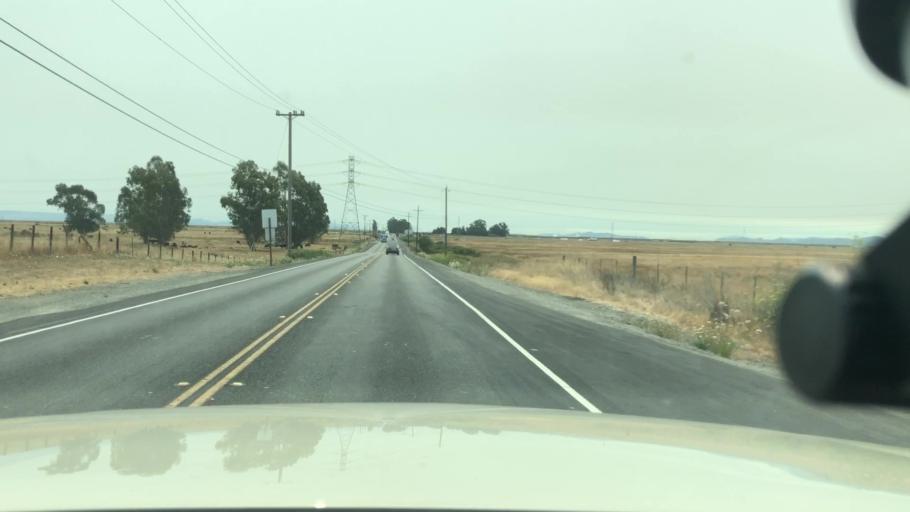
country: US
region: California
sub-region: Marin County
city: Black Point-Green Point
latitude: 38.1411
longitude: -122.4817
